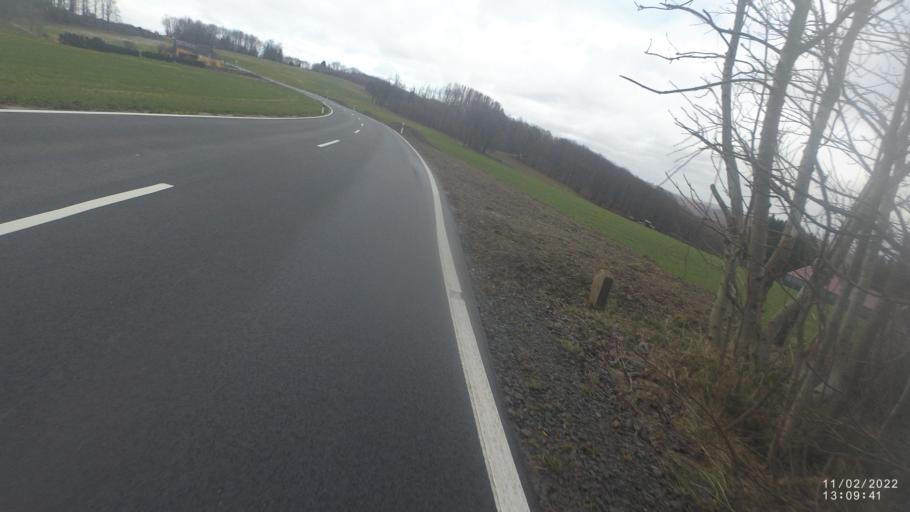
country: DE
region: North Rhine-Westphalia
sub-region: Regierungsbezirk Arnsberg
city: Nachrodt-Wiblingwerde
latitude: 51.3178
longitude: 7.6225
